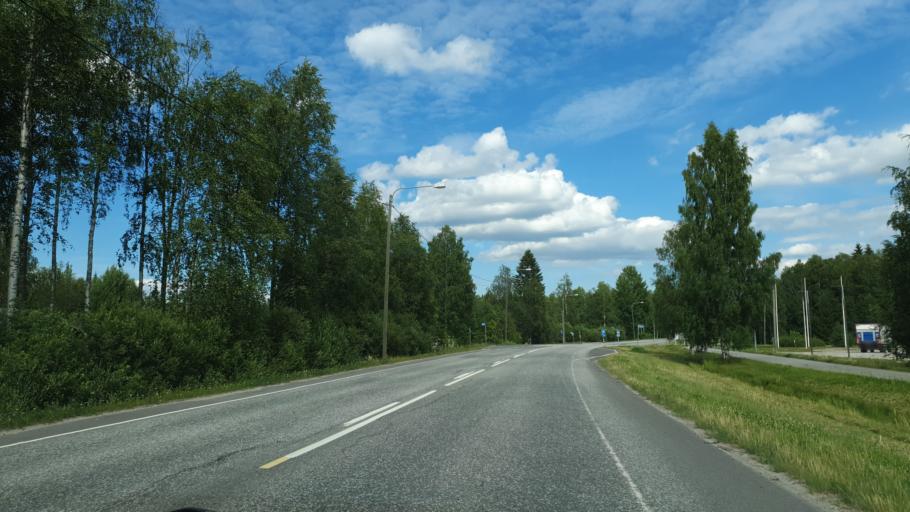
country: FI
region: Kainuu
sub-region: Kajaani
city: Kajaani
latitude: 64.2469
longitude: 27.7656
